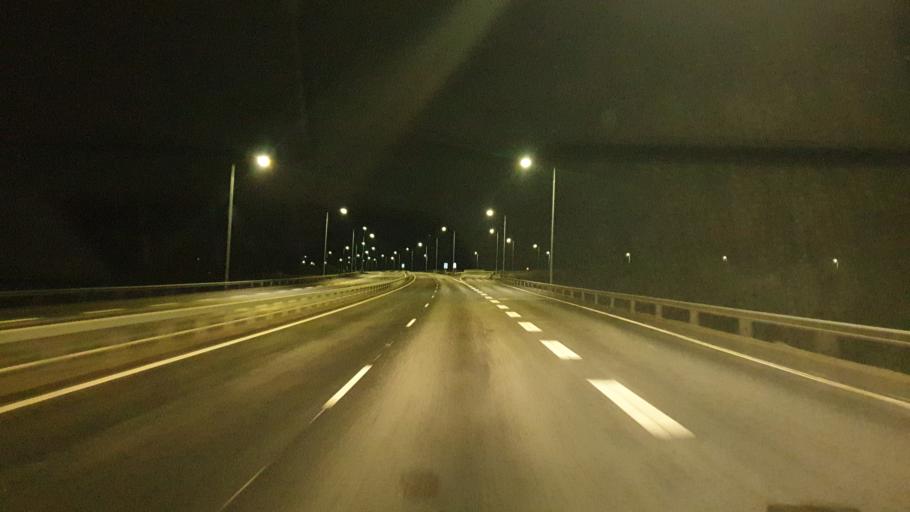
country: FI
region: Central Finland
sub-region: AEaenekoski
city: AEaenekoski
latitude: 62.6068
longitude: 25.6894
